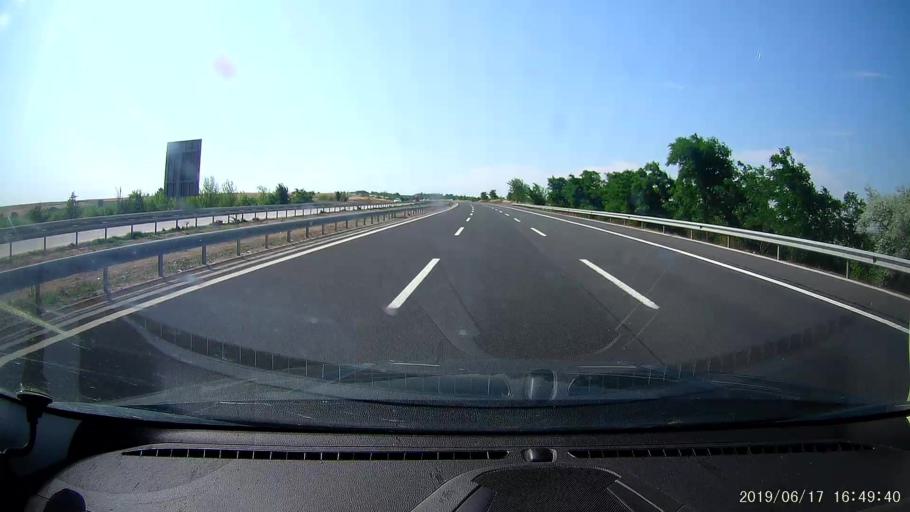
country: TR
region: Kirklareli
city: Babaeski
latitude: 41.5127
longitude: 27.1086
